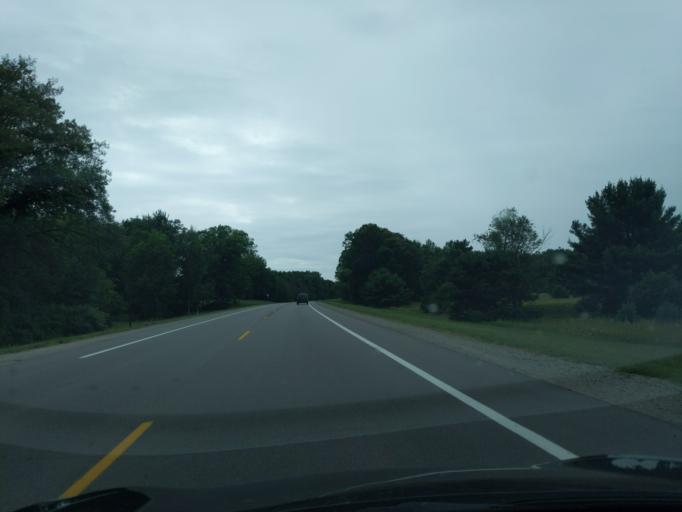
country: US
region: Michigan
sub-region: Clare County
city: Harrison
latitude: 44.0188
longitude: -84.8147
